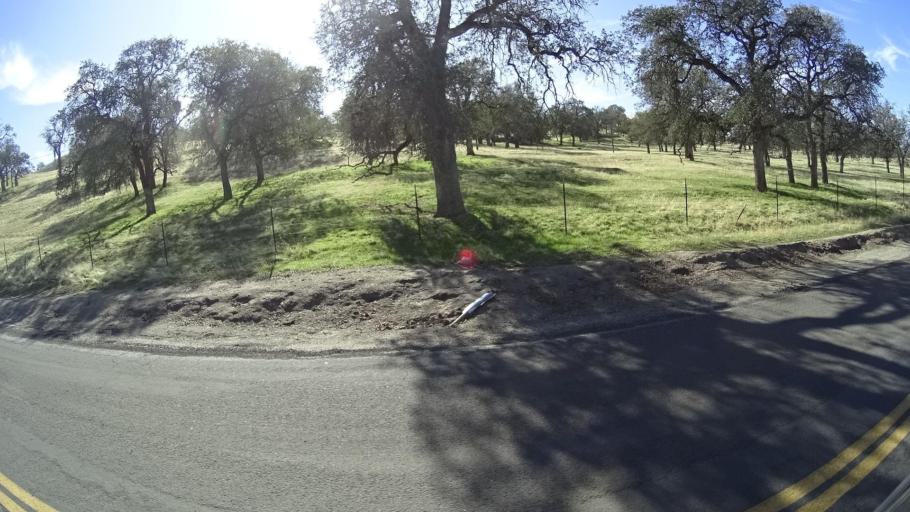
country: US
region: California
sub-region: Tulare County
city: Richgrove
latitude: 35.6996
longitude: -118.8438
